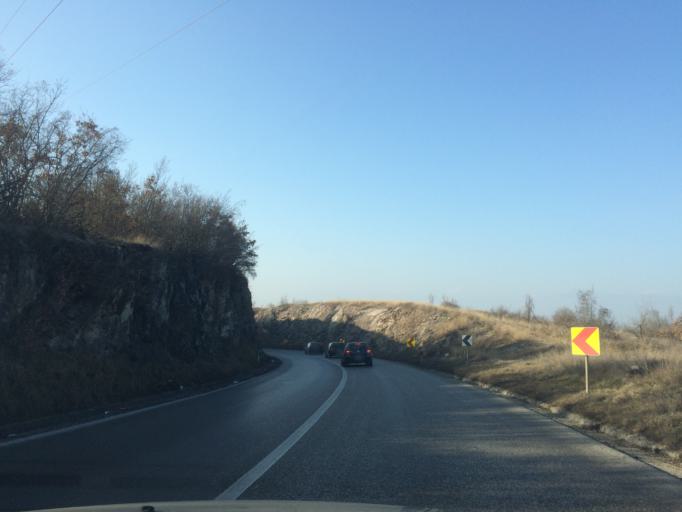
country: XK
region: Pec
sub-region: Komuna e Klines
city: Klina
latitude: 42.5970
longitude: 20.6069
